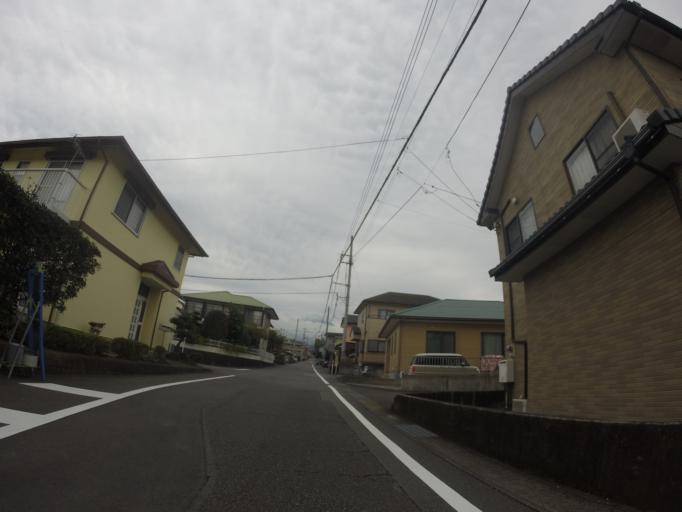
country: JP
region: Shizuoka
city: Fuji
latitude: 35.1925
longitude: 138.6774
